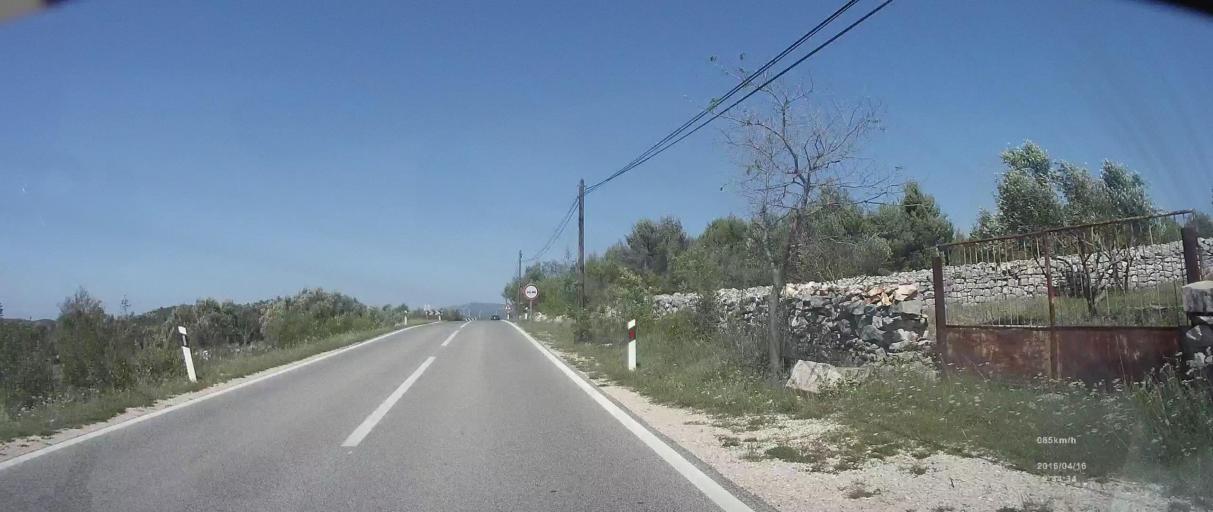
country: HR
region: Sibensko-Kniniska
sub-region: Grad Sibenik
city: Brodarica
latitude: 43.6426
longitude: 16.0637
